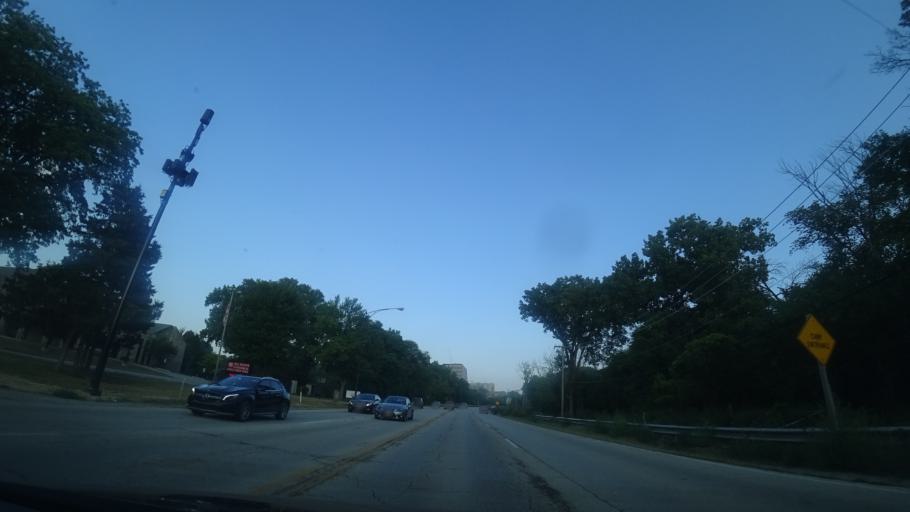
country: US
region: Illinois
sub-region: Cook County
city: Park Ridge
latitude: 41.9886
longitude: -87.8526
